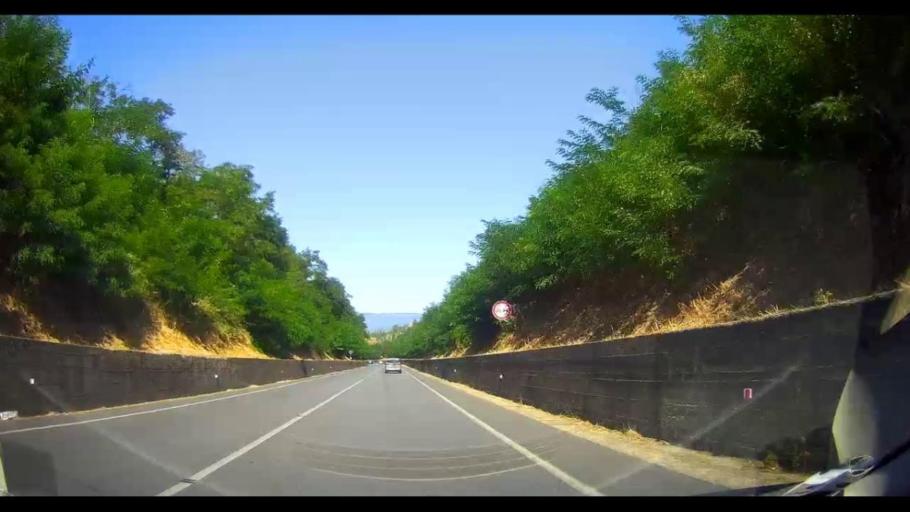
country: IT
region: Calabria
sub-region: Provincia di Cosenza
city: Zumpano
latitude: 39.2972
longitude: 16.3025
